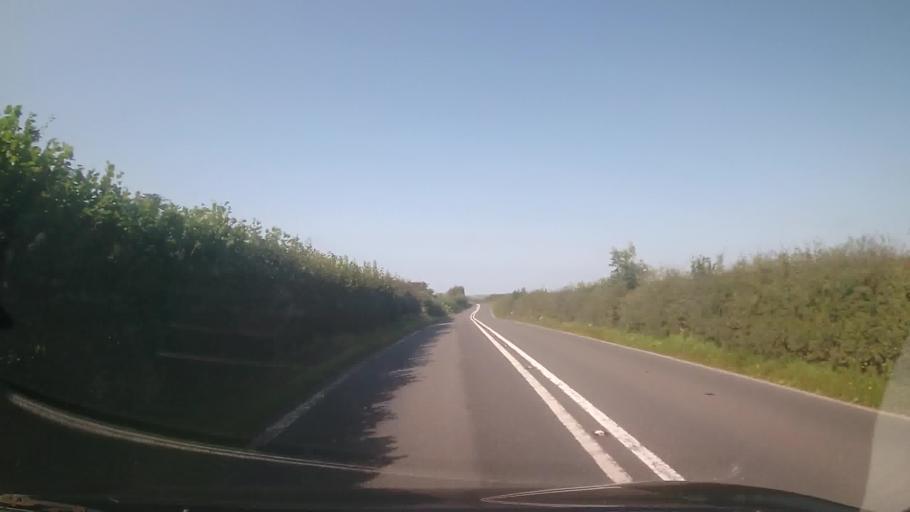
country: GB
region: Wales
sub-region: Sir Powys
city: Builth Wells
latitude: 52.1509
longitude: -3.4455
